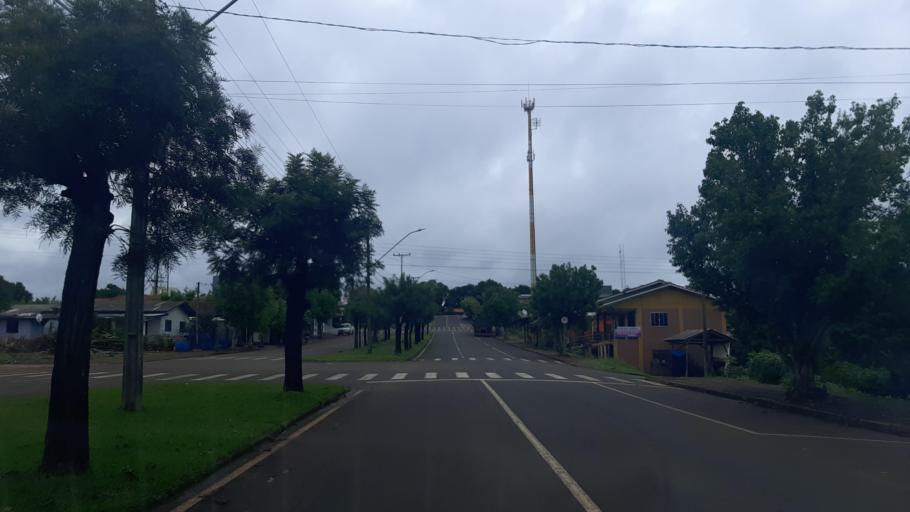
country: BR
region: Parana
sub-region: Ampere
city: Ampere
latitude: -25.9249
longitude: -53.4716
